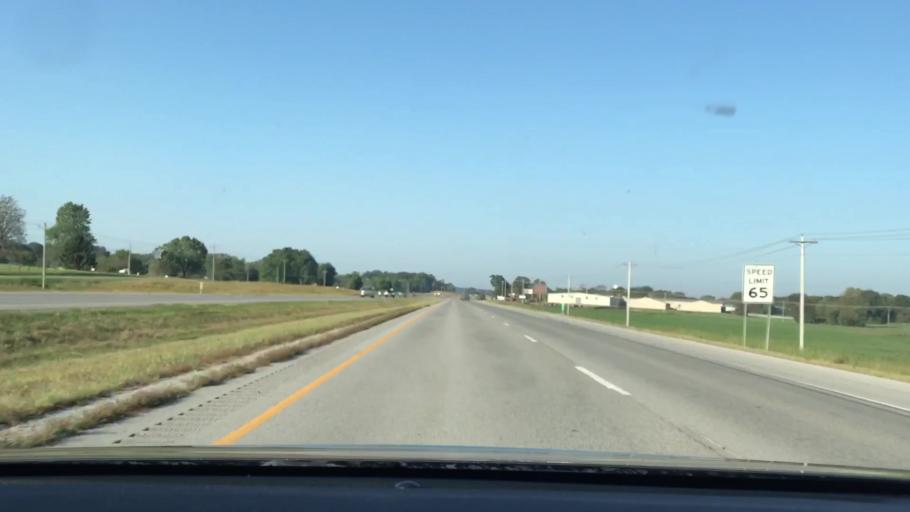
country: US
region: Kentucky
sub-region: Trigg County
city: Cadiz
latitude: 36.8745
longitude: -87.7566
